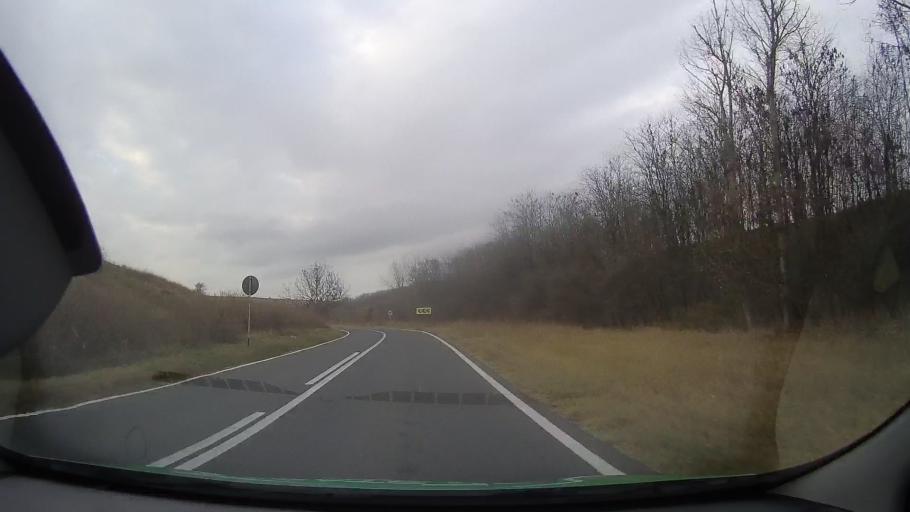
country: RO
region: Constanta
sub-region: Comuna Deleni
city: Deleni
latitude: 44.1001
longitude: 28.0294
